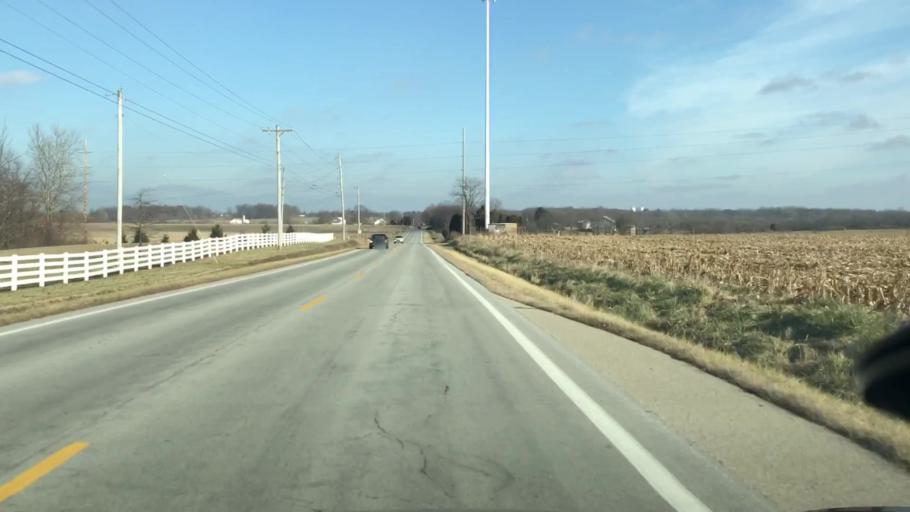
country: US
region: Ohio
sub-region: Greene County
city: Yellow Springs
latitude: 39.7954
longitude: -83.9366
